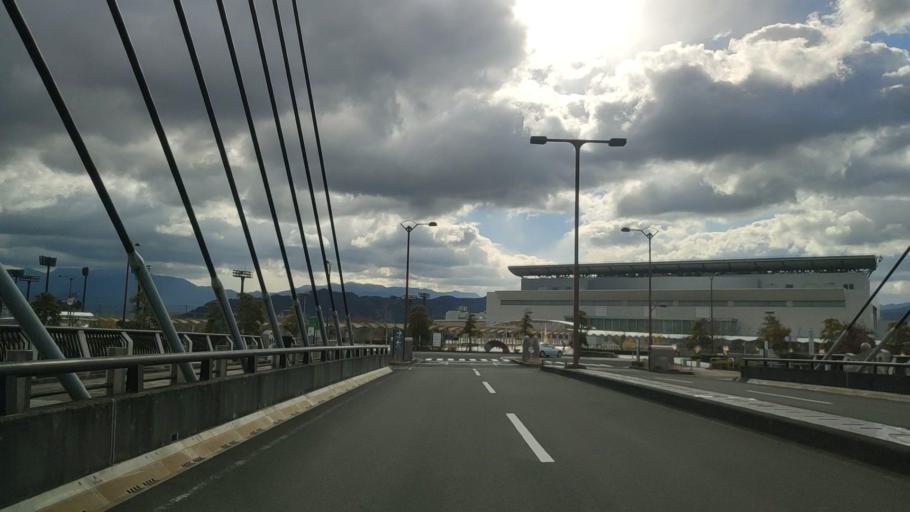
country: JP
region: Ehime
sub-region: Shikoku-chuo Shi
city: Matsuyama
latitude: 33.8105
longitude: 132.7420
